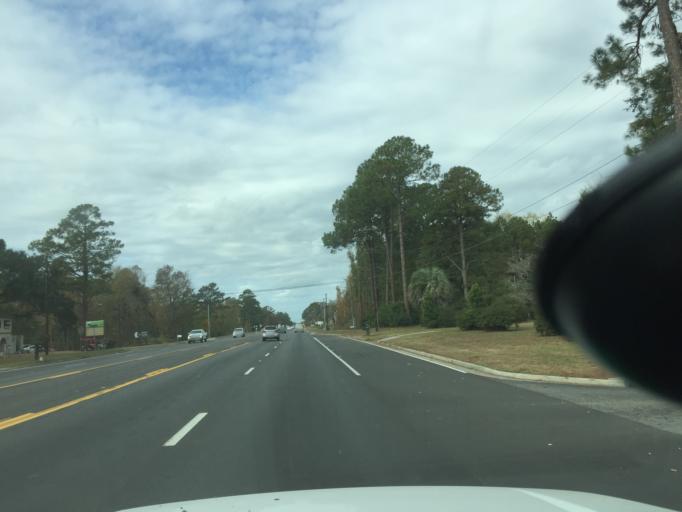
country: US
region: Georgia
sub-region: Chatham County
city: Garden City
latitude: 32.0863
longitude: -81.1677
